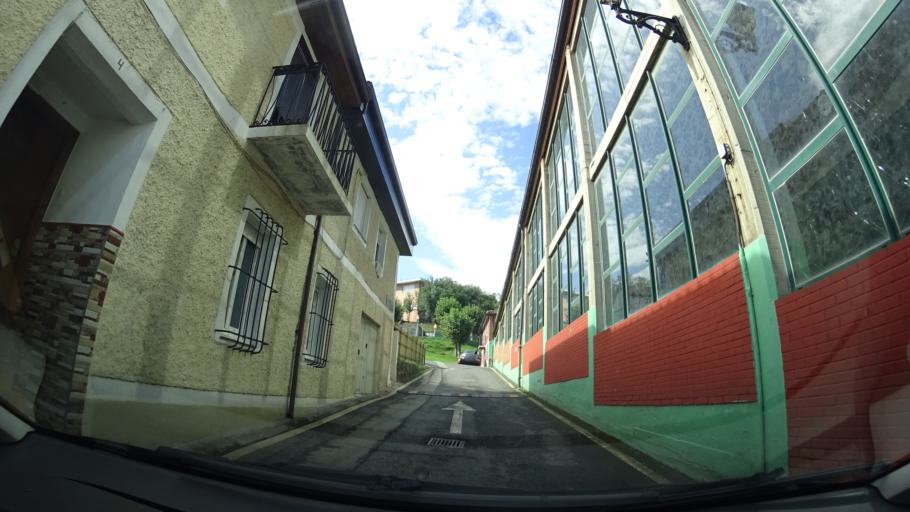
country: ES
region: Basque Country
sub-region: Bizkaia
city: Urtuella
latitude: 43.2844
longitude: -3.0553
